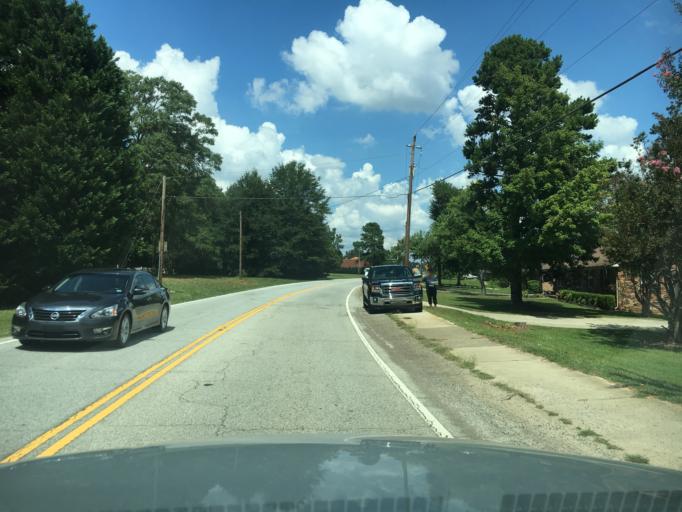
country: US
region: South Carolina
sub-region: Spartanburg County
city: Fairforest
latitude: 34.9129
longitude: -82.0054
